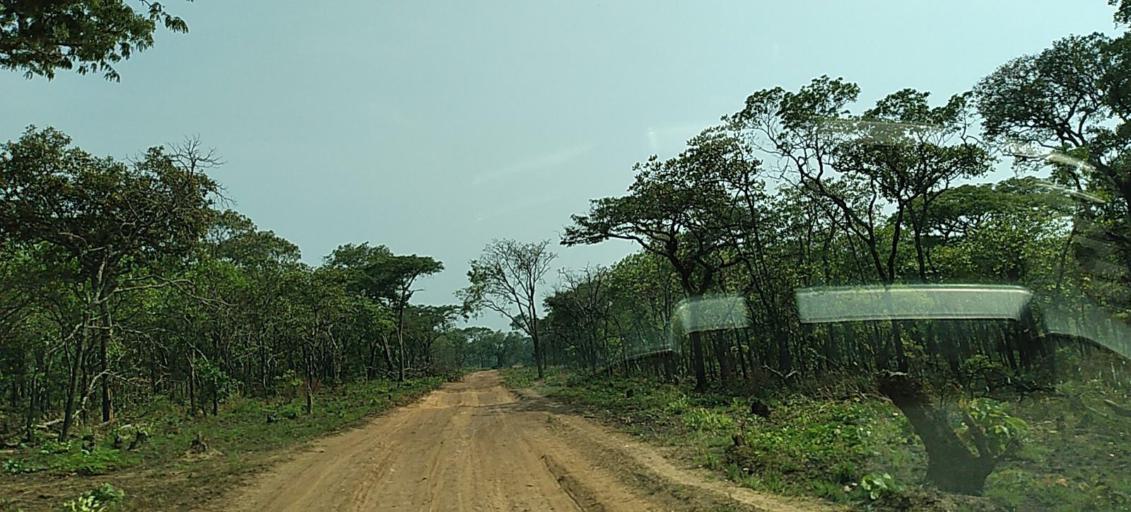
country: ZM
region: North-Western
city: Kansanshi
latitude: -12.0879
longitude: 26.8880
